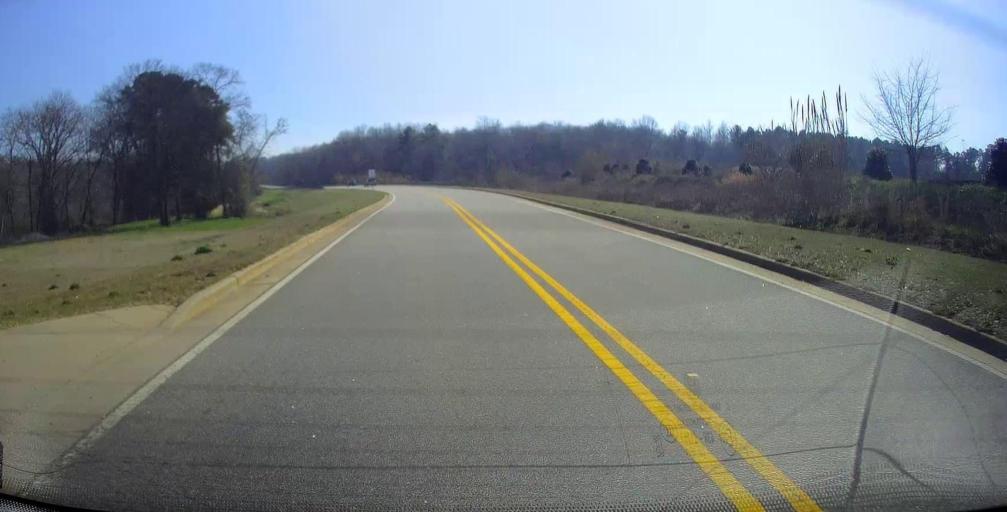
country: US
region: Georgia
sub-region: Houston County
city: Perry
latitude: 32.4485
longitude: -83.7298
